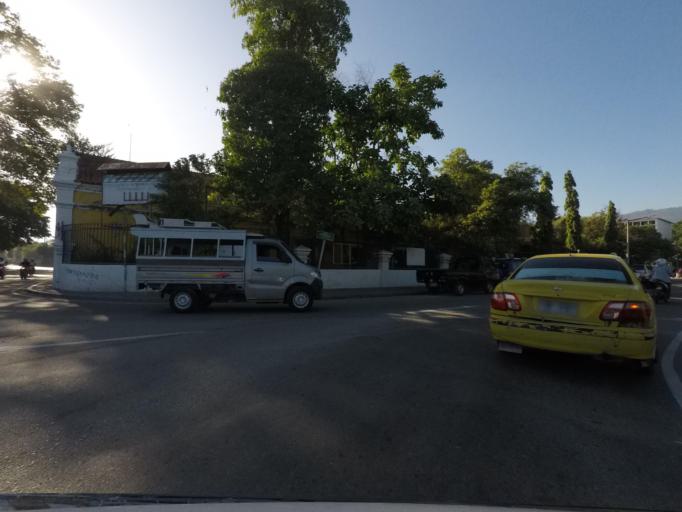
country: TL
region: Dili
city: Dili
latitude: -8.5531
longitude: 125.5792
